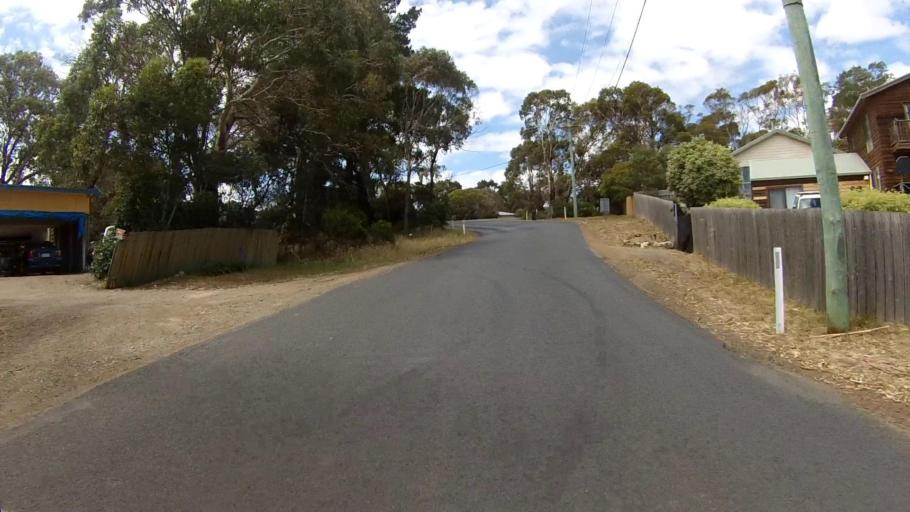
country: AU
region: Tasmania
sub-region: Sorell
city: Sorell
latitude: -42.8701
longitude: 147.6435
